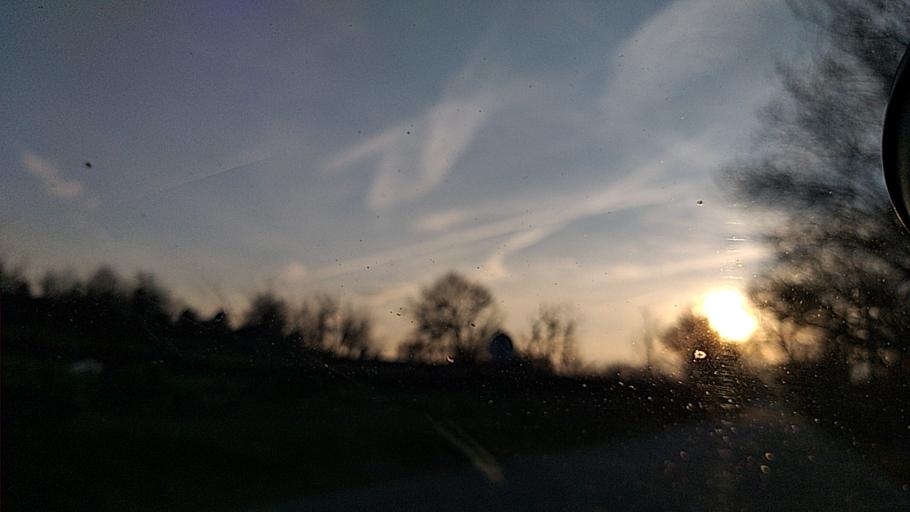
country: PT
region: Guarda
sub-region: Guarda
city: Sequeira
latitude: 40.6038
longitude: -7.0781
